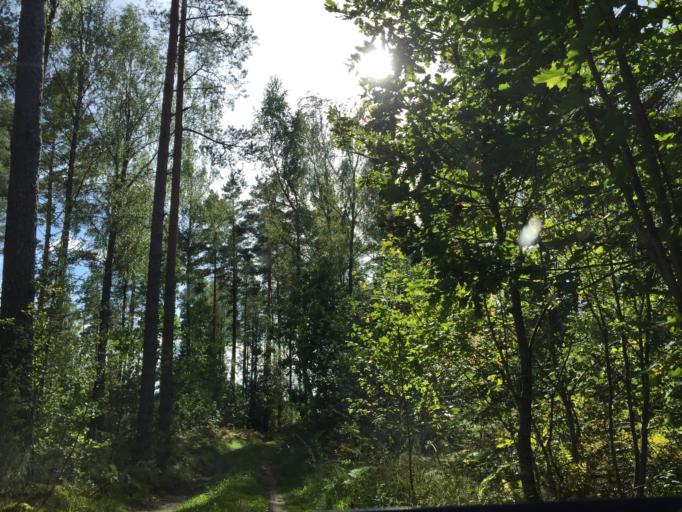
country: LV
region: Kuldigas Rajons
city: Kuldiga
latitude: 56.9944
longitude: 21.8160
